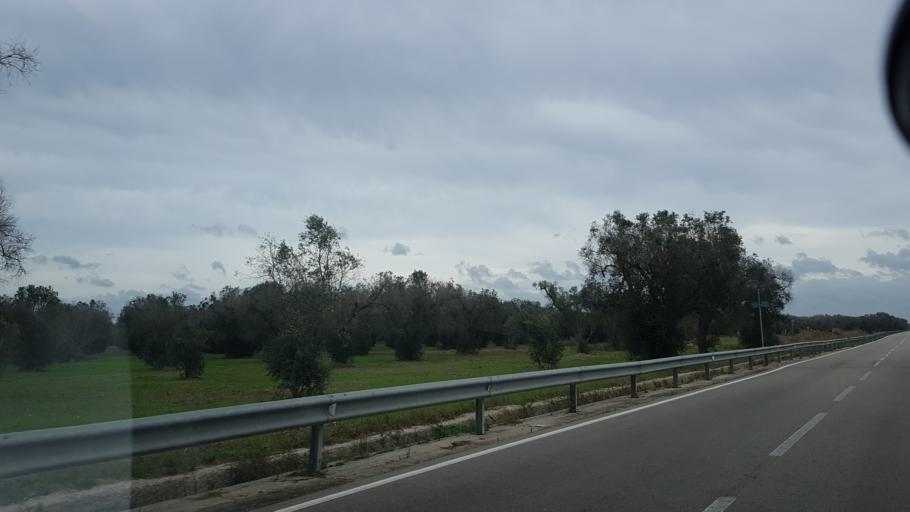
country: IT
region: Apulia
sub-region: Provincia di Brindisi
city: San Pancrazio Salentino
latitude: 40.4079
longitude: 17.8821
